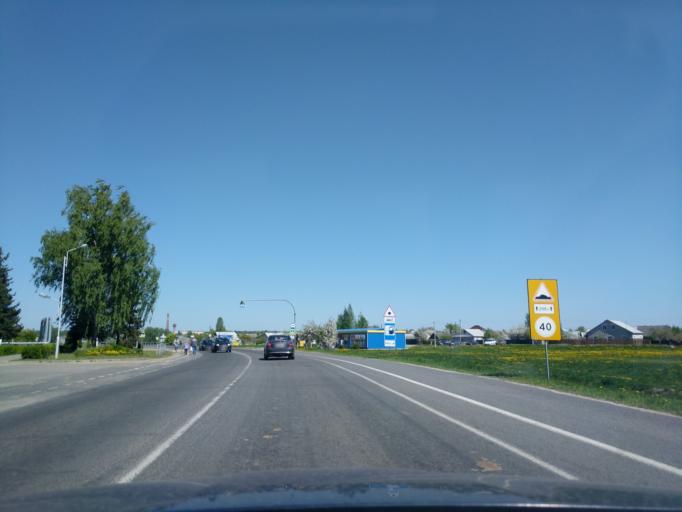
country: BY
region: Minsk
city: Myadzyel
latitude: 54.8754
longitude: 26.9413
